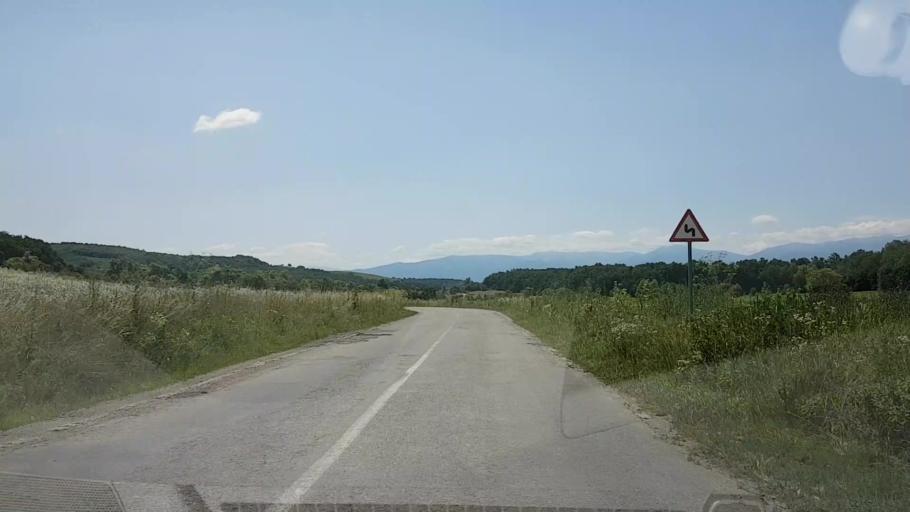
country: RO
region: Brasov
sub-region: Comuna Cincu
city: Cincu
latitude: 45.8787
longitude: 24.8155
